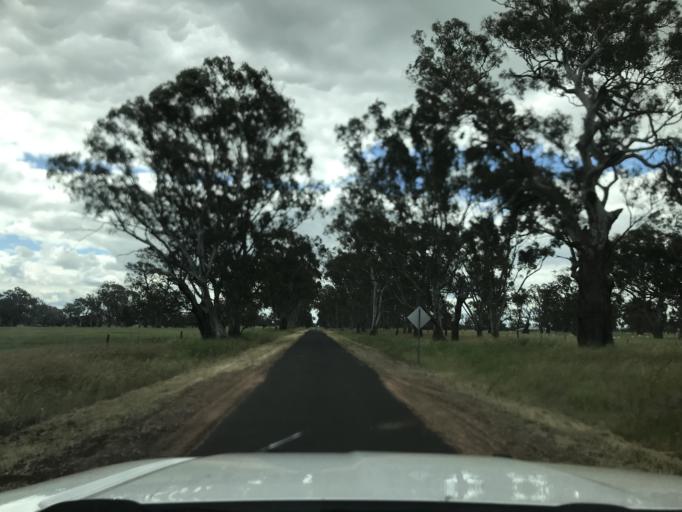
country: AU
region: South Australia
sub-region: Wattle Range
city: Penola
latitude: -37.0781
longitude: 141.1821
